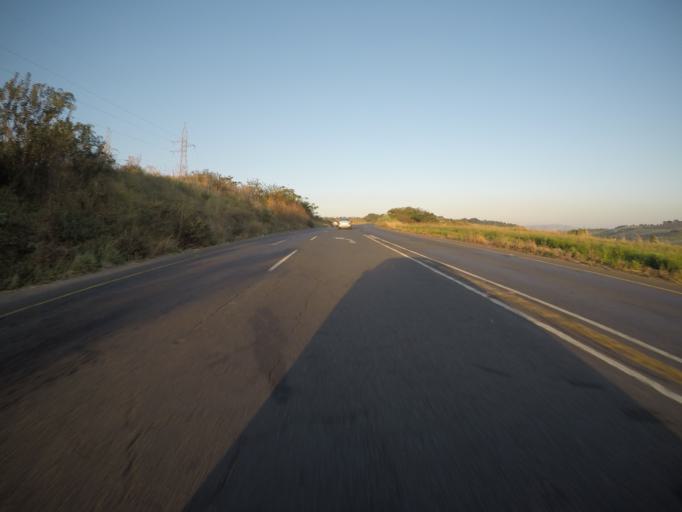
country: ZA
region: KwaZulu-Natal
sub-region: uThungulu District Municipality
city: eSikhawini
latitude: -28.8200
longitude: 31.8842
